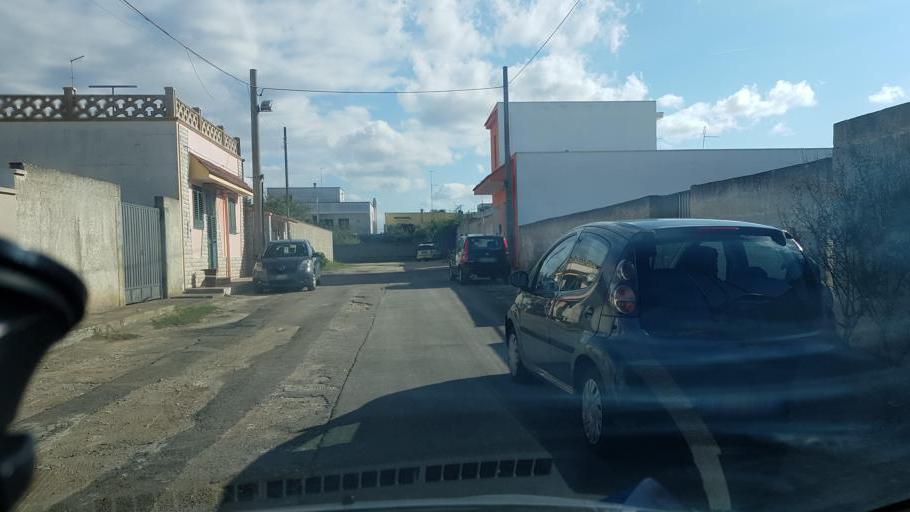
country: IT
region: Apulia
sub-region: Provincia di Brindisi
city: San Pietro Vernotico
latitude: 40.4880
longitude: 17.9890
